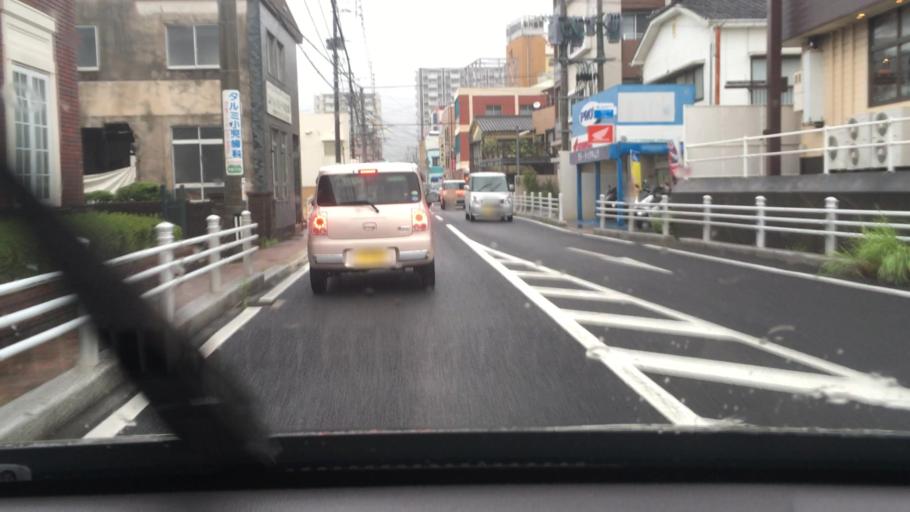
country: JP
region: Nagasaki
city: Sasebo
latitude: 33.1322
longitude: 129.7984
